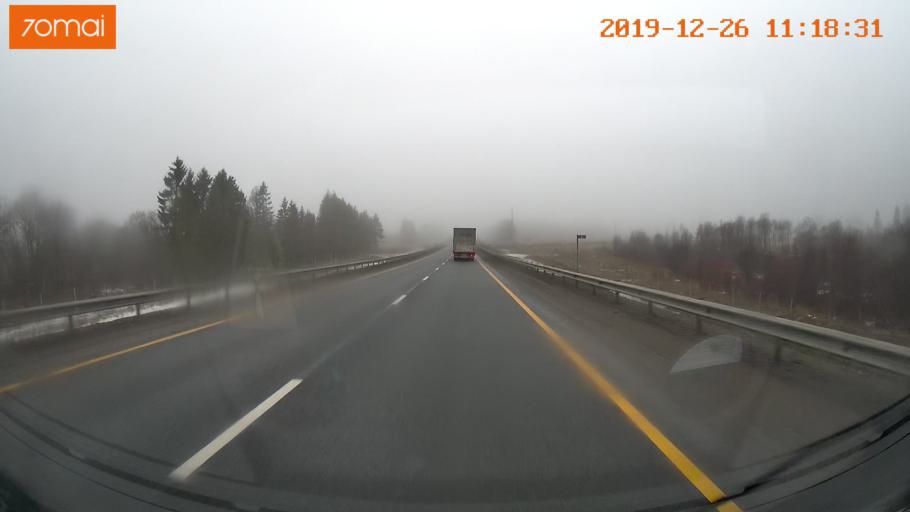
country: RU
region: Vologda
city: Chebsara
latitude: 59.1192
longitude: 39.0322
